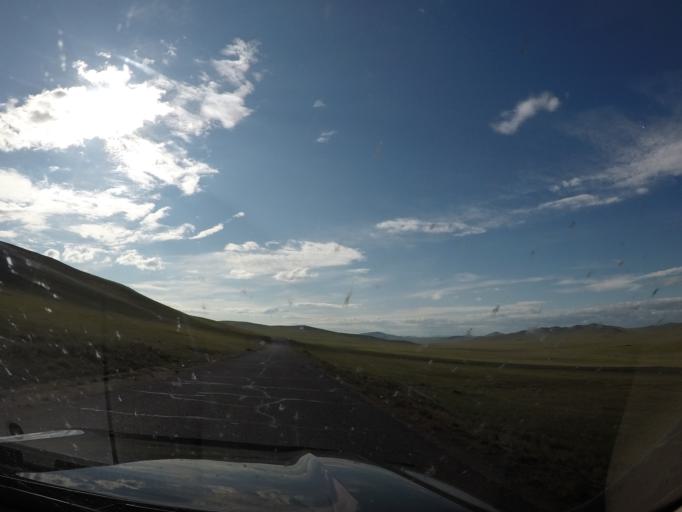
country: MN
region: Hentiy
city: Modot
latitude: 47.8092
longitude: 108.8010
